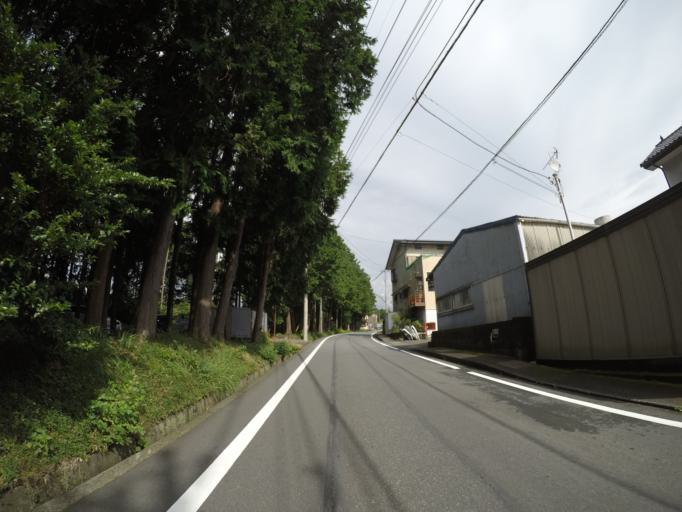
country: JP
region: Shizuoka
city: Fuji
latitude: 35.2078
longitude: 138.6707
